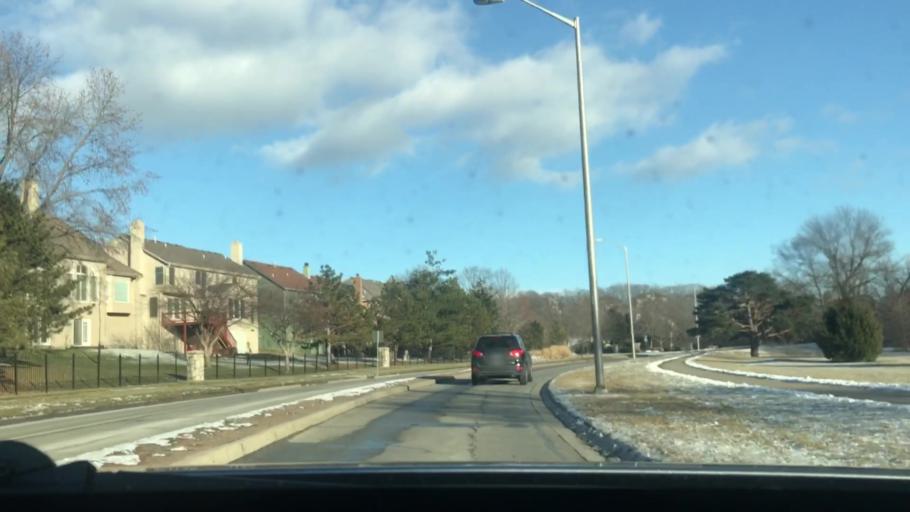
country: US
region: Kansas
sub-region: Johnson County
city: Lenexa
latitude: 38.9952
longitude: -94.7417
